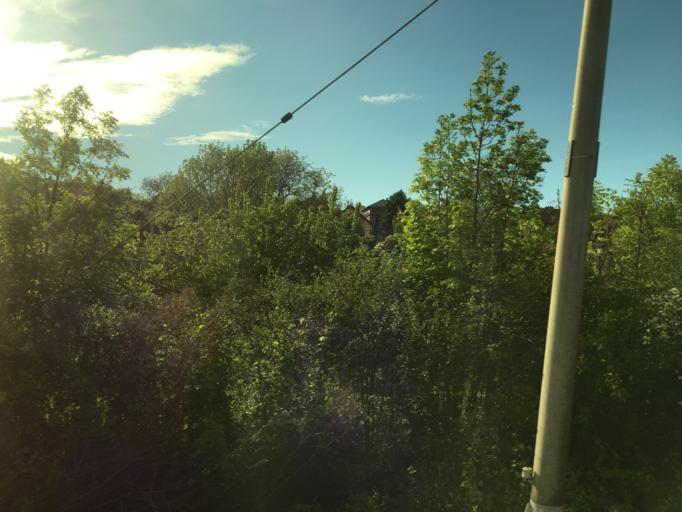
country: CZ
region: Ustecky
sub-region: Okres Decin
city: Decin
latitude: 50.7531
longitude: 14.1852
